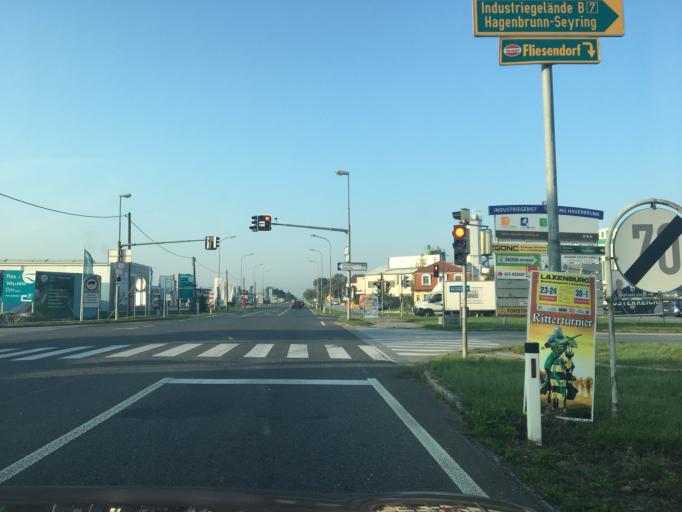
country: AT
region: Lower Austria
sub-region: Politischer Bezirk Mistelbach
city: Grossebersdorf
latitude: 48.3316
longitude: 16.4547
